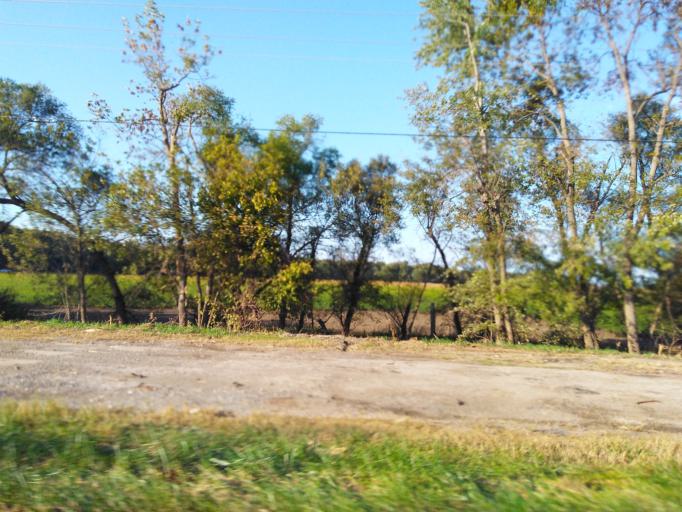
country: US
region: Illinois
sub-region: Madison County
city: Saint Jacob
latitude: 38.7161
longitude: -89.8251
